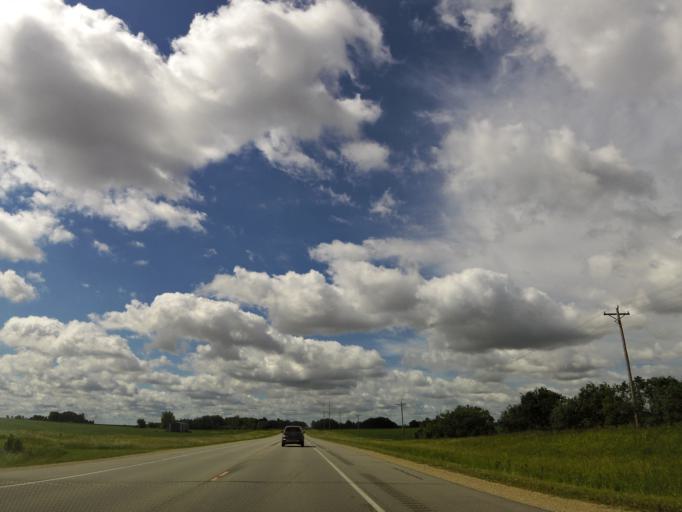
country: US
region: Minnesota
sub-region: Olmsted County
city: Stewartville
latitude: 43.8279
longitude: -92.4893
